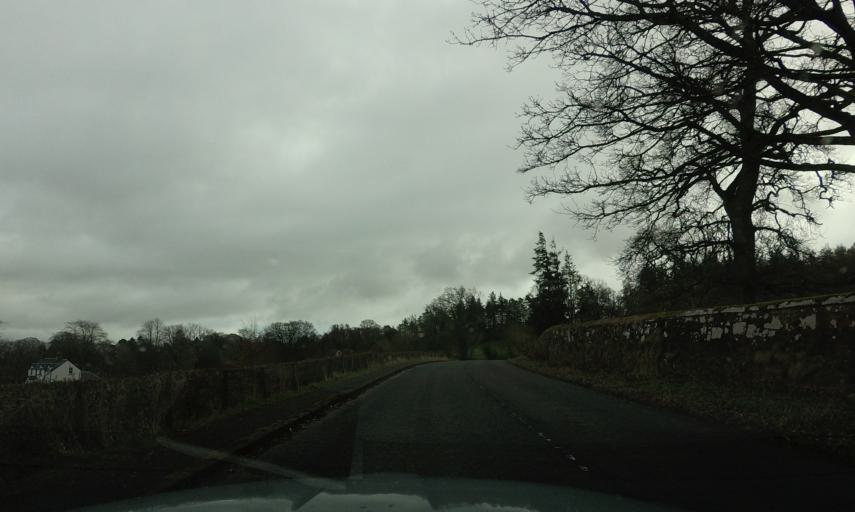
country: GB
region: Scotland
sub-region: Stirling
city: Callander
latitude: 56.1297
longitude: -4.1874
